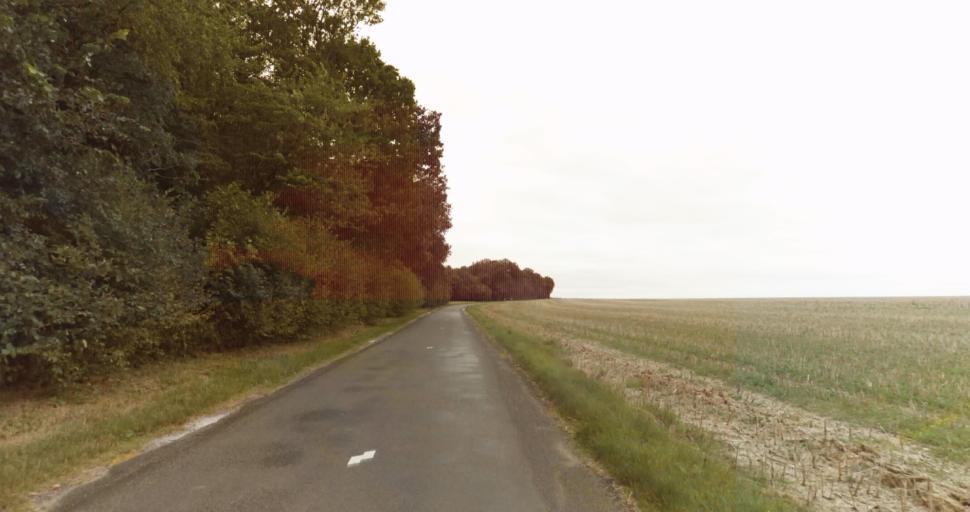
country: FR
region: Haute-Normandie
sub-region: Departement de l'Eure
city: Evreux
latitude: 48.9610
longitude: 1.2463
